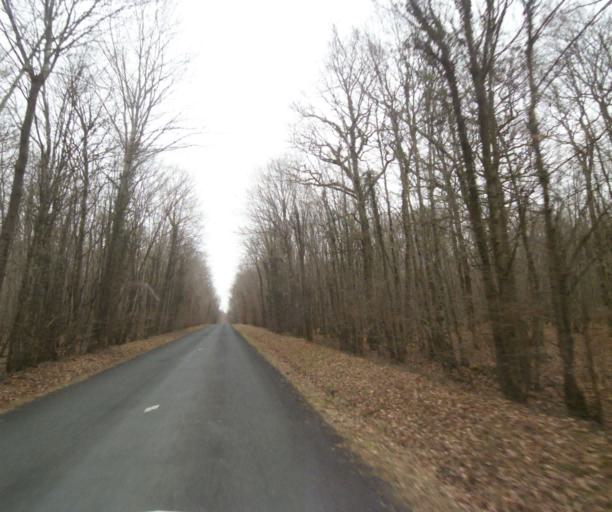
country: FR
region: Champagne-Ardenne
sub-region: Departement de la Haute-Marne
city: Bienville
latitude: 48.5595
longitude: 5.0039
